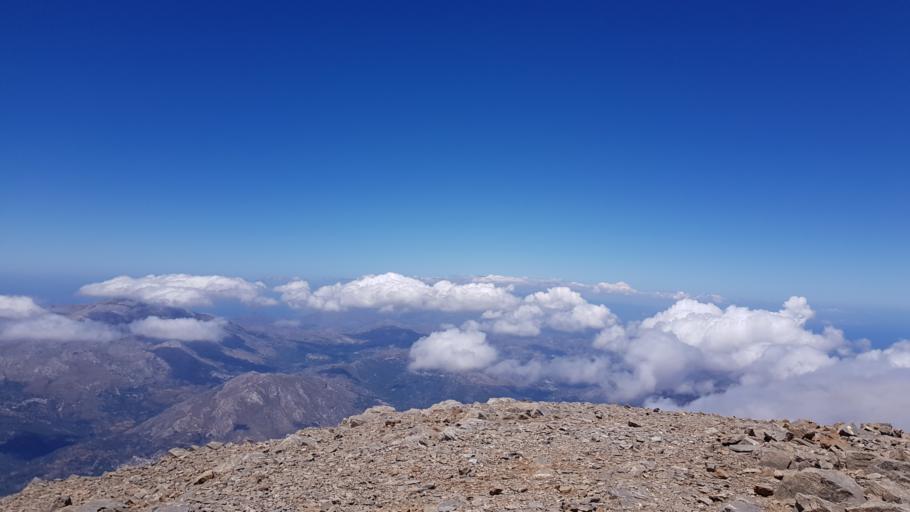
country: GR
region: Crete
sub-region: Nomos Rethymnis
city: Zoniana
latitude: 35.2264
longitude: 24.7707
